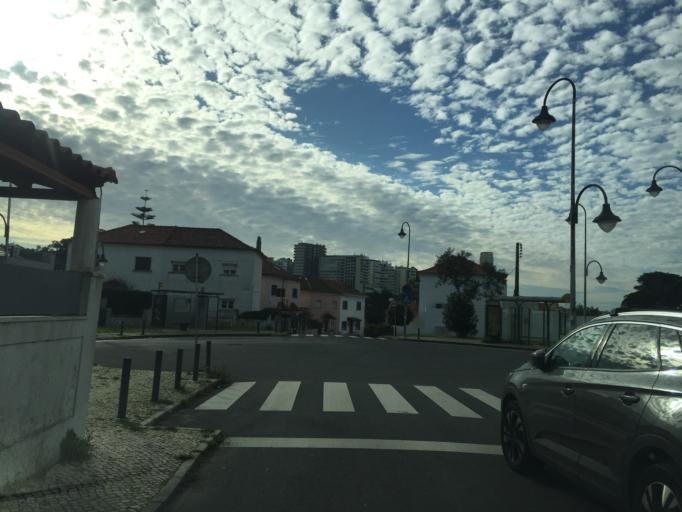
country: PT
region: Lisbon
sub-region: Oeiras
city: Alges
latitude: 38.7173
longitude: -9.2130
